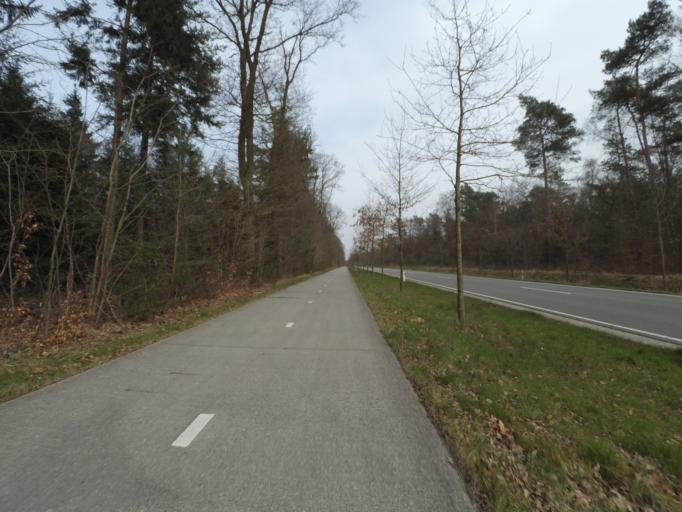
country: NL
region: Gelderland
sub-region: Gemeente Arnhem
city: Hoogkamp
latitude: 52.0325
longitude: 5.8520
